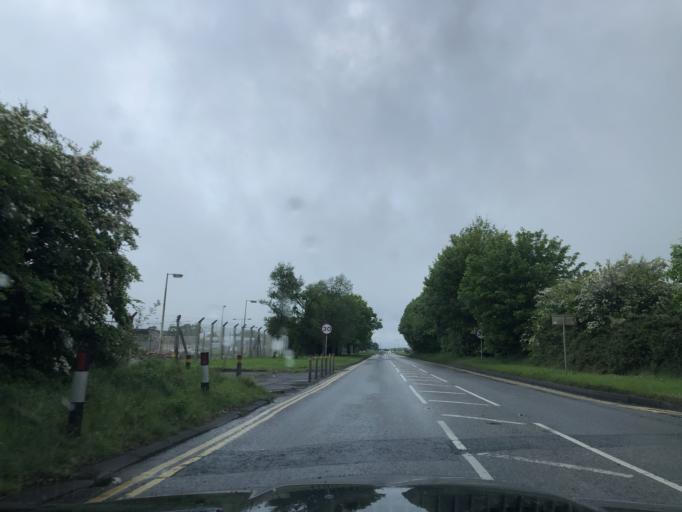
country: GB
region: Northern Ireland
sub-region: Antrim Borough
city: Antrim
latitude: 54.6652
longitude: -6.2074
